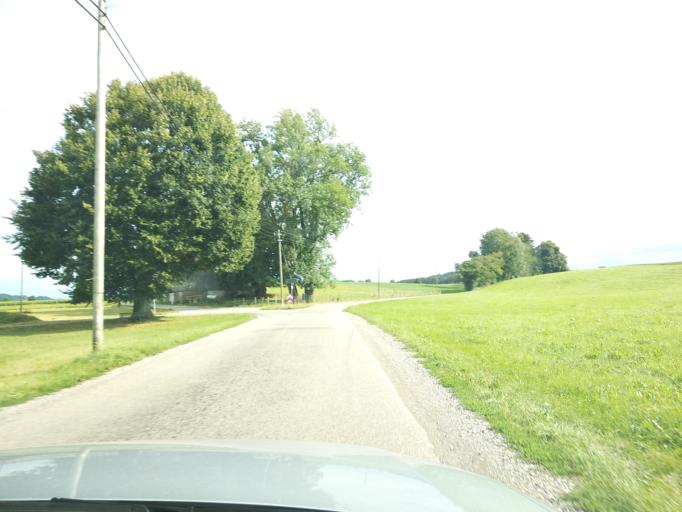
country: DE
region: Bavaria
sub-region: Swabia
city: Wolfertschwenden
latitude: 47.8840
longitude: 10.2305
